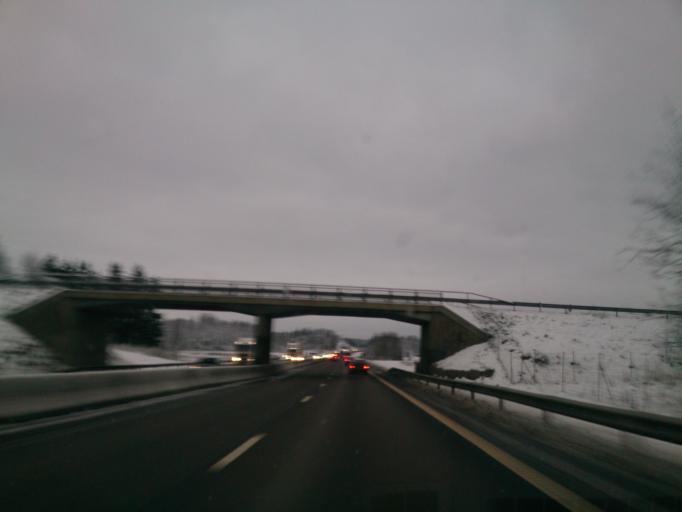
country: SE
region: OEstergoetland
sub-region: Norrkopings Kommun
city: Kimstad
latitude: 58.5245
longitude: 16.0101
